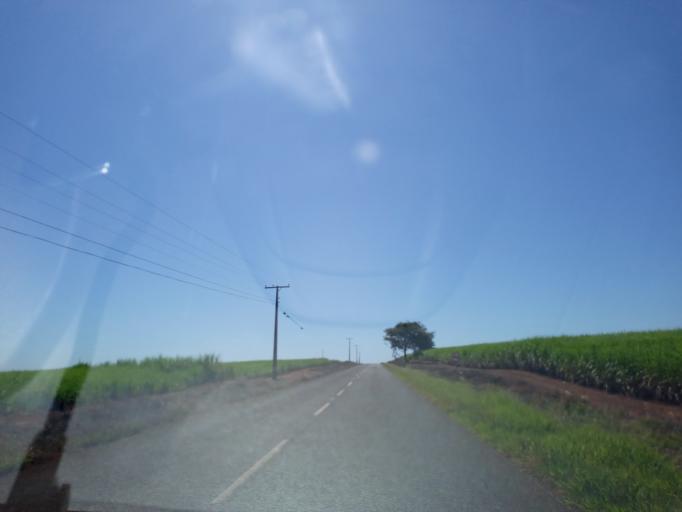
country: BR
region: Goias
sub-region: Itumbiara
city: Itumbiara
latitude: -18.4250
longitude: -49.1693
